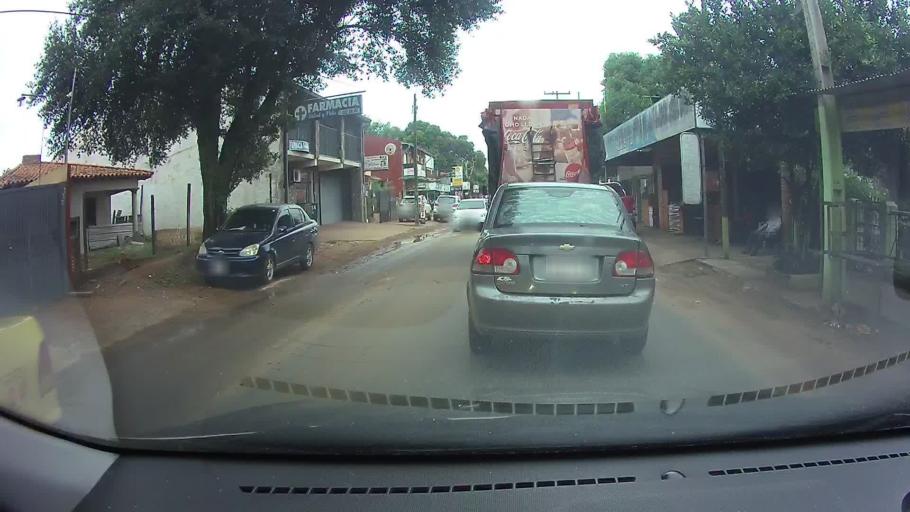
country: PY
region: Central
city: San Lorenzo
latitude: -25.3272
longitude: -57.5037
